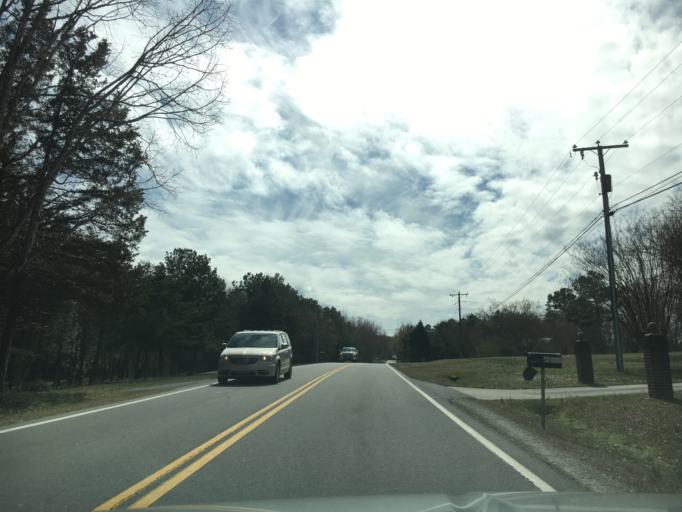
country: US
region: Virginia
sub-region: Halifax County
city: Halifax
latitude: 36.7531
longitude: -78.9185
